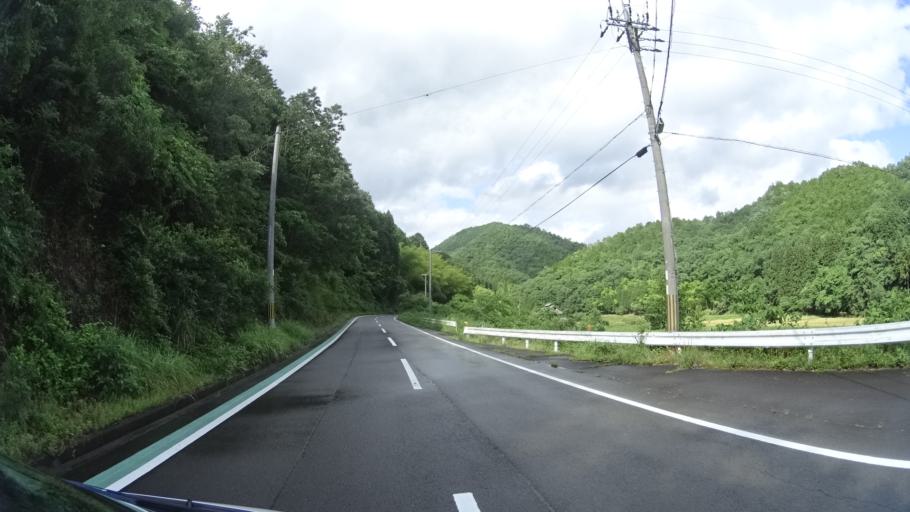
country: JP
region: Kyoto
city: Ayabe
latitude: 35.3827
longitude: 135.2554
